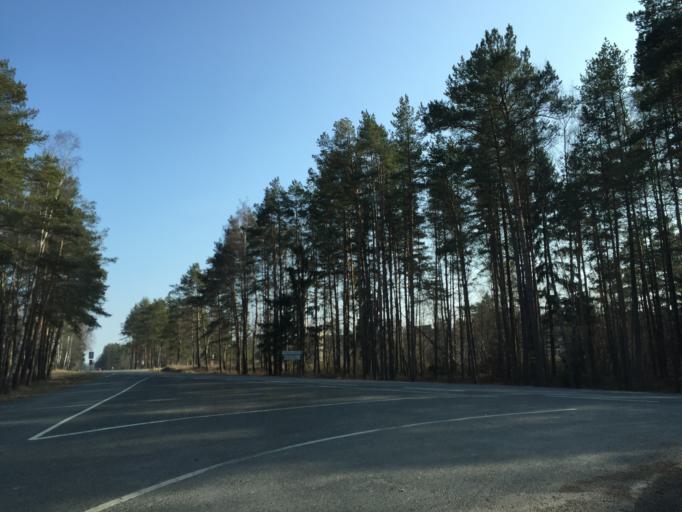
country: EE
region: Saare
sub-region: Orissaare vald
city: Orissaare
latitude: 58.5998
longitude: 23.3197
